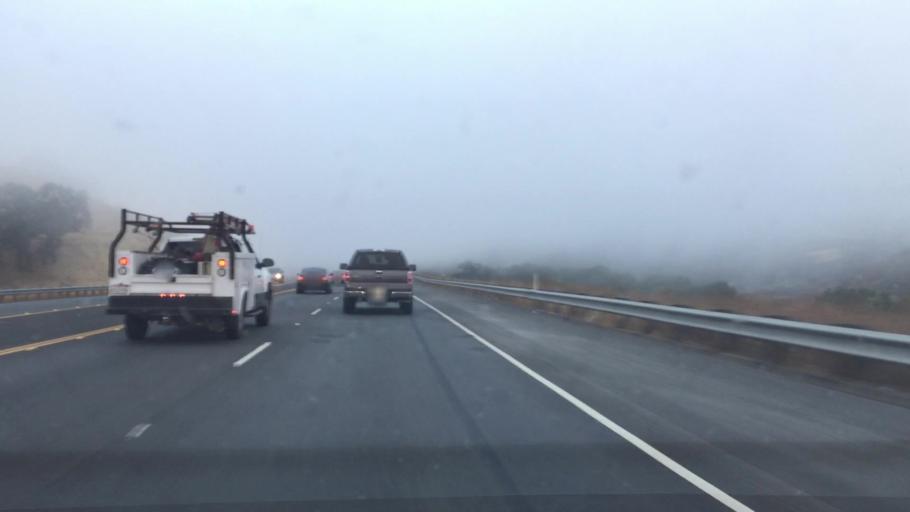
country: US
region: California
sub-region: Alameda County
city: Livermore
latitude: 37.6263
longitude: -121.8052
